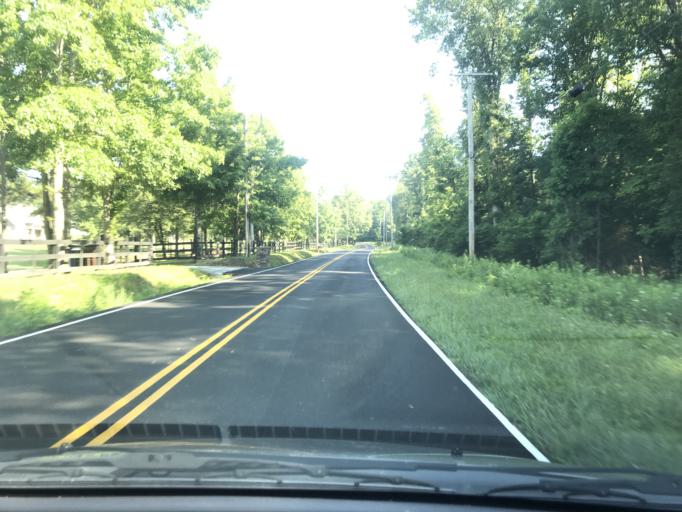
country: US
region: Tennessee
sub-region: Loudon County
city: Loudon
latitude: 35.7969
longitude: -84.3633
